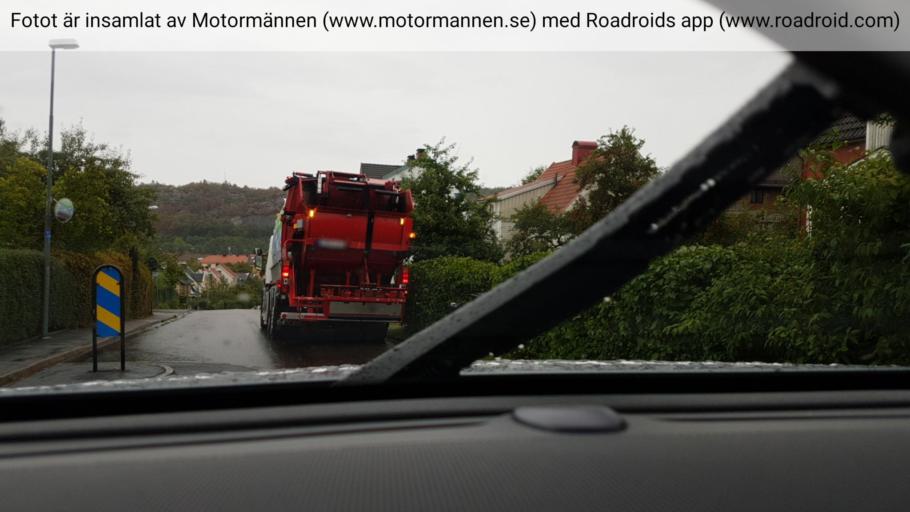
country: SE
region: Vaestra Goetaland
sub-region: Molndal
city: Moelndal
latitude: 57.6734
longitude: 12.0007
